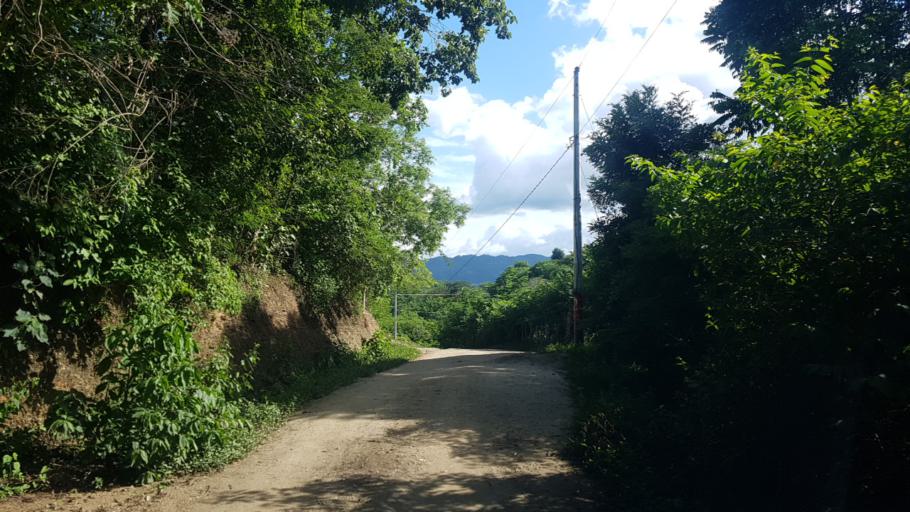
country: NI
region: Nueva Segovia
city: Mozonte
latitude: 13.6437
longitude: -86.3975
